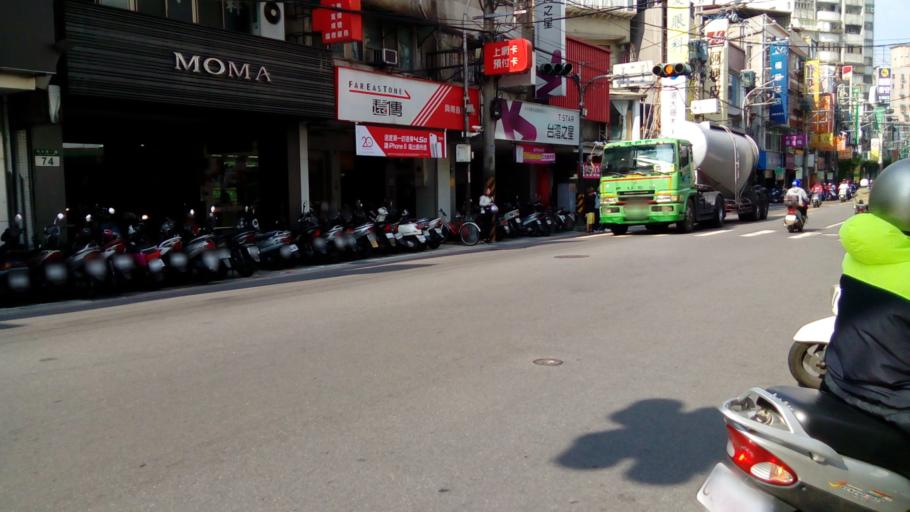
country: TW
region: Taipei
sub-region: Taipei
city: Banqiao
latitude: 24.9901
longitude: 121.5104
